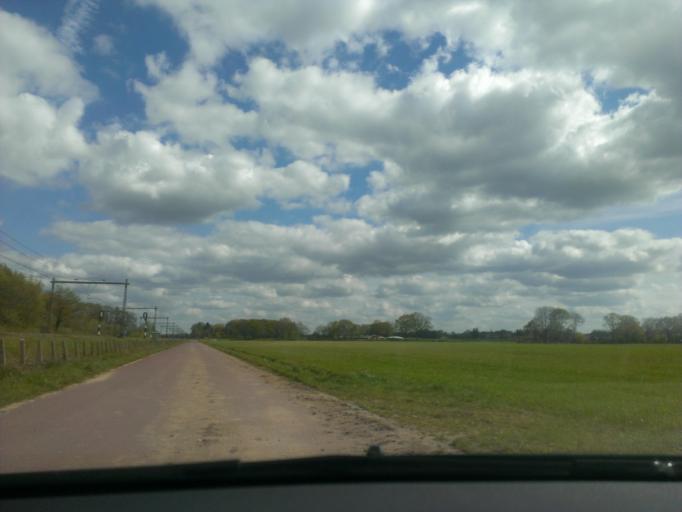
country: NL
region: Overijssel
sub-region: Gemeente Borne
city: Borne
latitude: 52.3210
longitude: 6.7070
